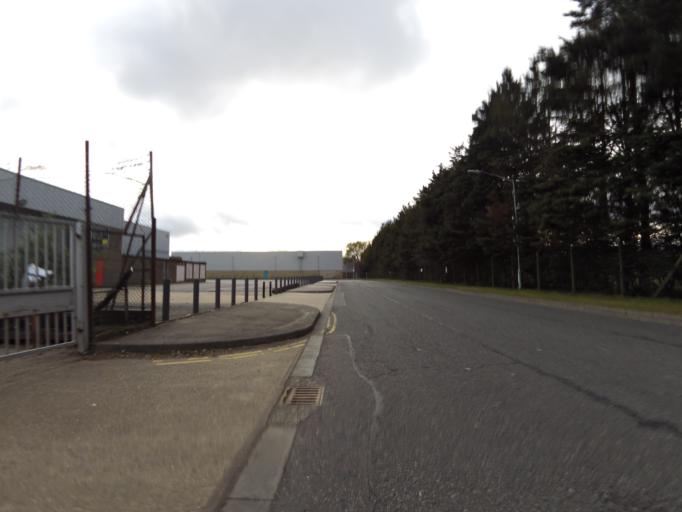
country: GB
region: England
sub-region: Suffolk
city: Kesgrave
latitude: 52.0303
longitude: 1.2058
